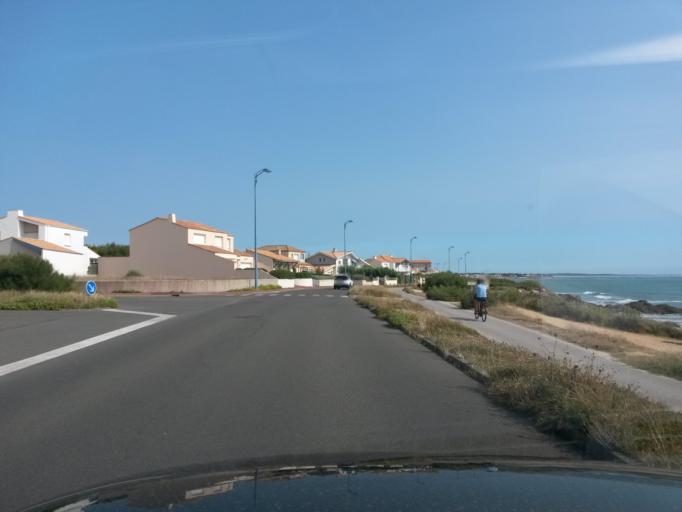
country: FR
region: Pays de la Loire
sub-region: Departement de la Vendee
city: Bretignolles-sur-Mer
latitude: 46.6344
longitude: -1.8883
